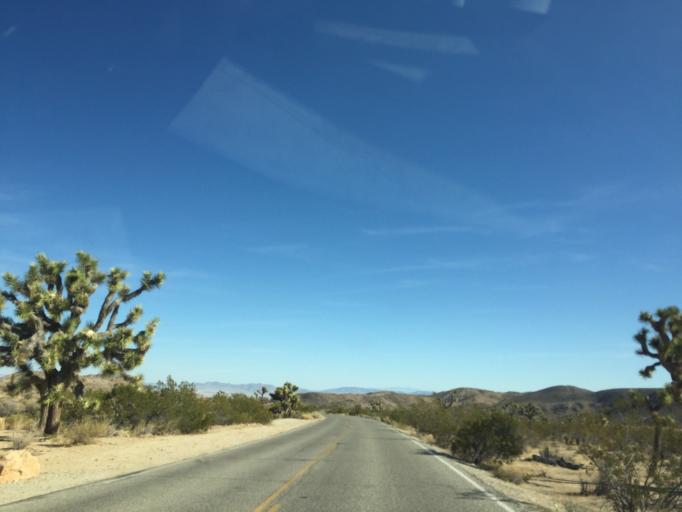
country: US
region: California
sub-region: San Bernardino County
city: Twentynine Palms
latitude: 34.0083
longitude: -116.0202
